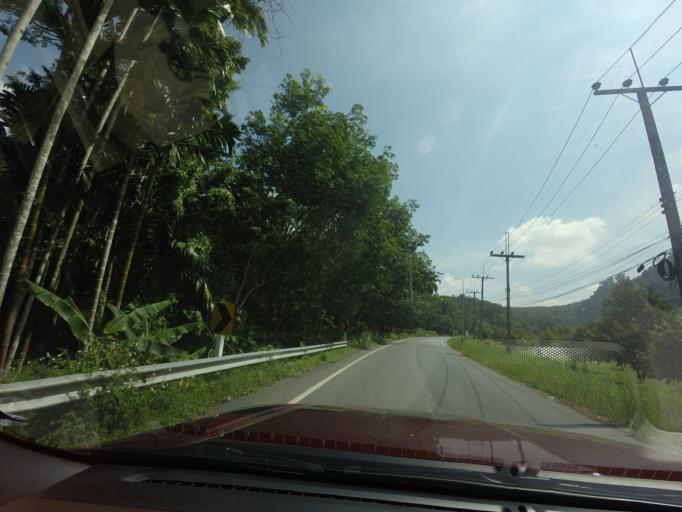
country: TH
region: Yala
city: Betong
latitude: 5.8284
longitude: 101.0784
